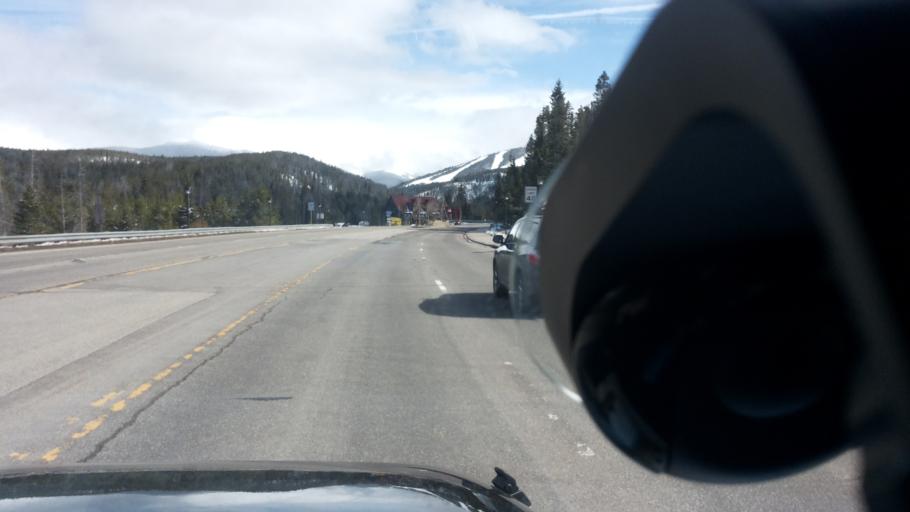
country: US
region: Colorado
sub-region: Grand County
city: Fraser
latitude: 39.9164
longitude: -105.7834
